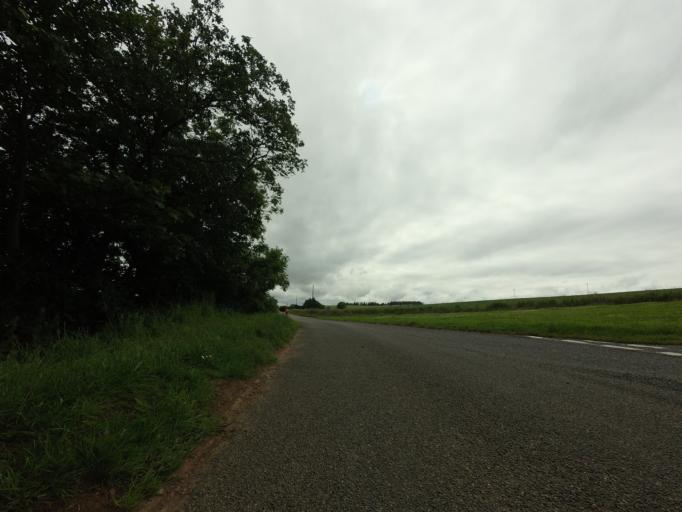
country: GB
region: Scotland
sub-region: Aberdeenshire
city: Turriff
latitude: 57.5417
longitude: -2.3656
